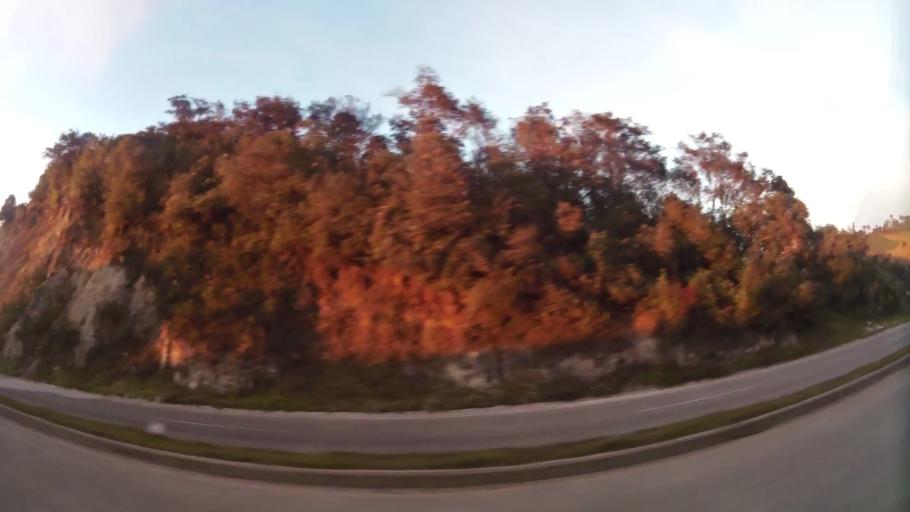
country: GT
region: Solola
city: Concepcion
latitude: 14.8331
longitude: -91.1127
